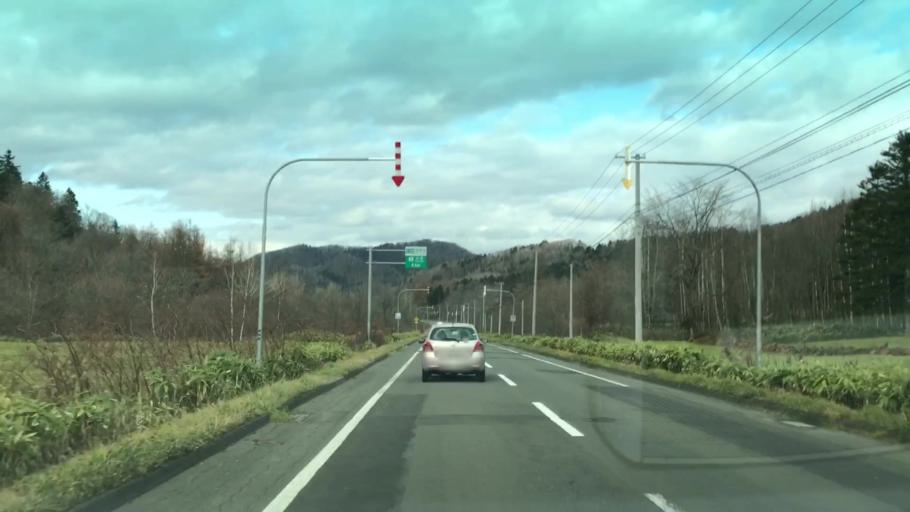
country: JP
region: Hokkaido
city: Shimo-furano
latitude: 42.9350
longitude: 142.4449
